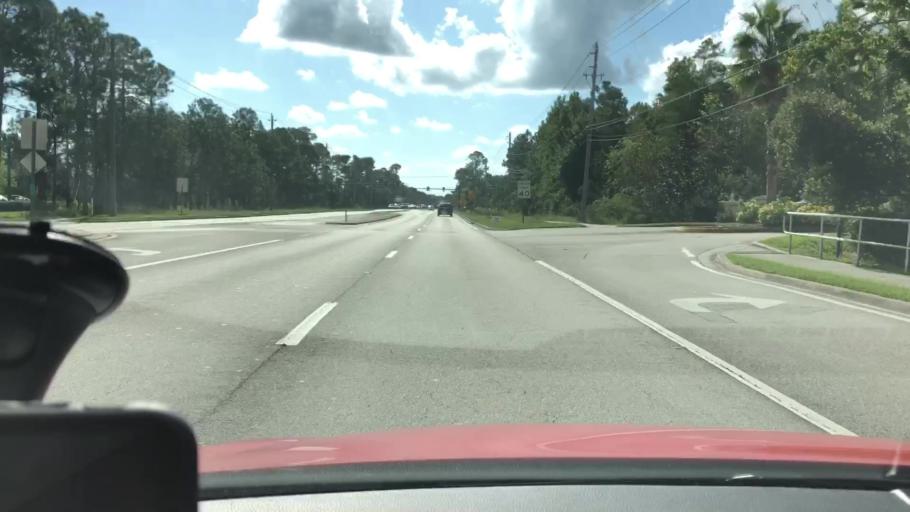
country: US
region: Florida
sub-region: Volusia County
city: Ormond Beach
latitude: 29.2515
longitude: -81.1109
